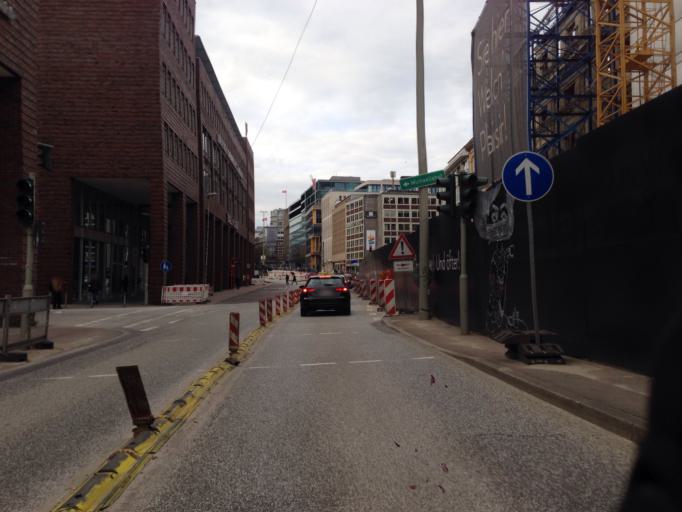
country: DE
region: Hamburg
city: Neustadt
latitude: 53.5508
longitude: 9.9858
